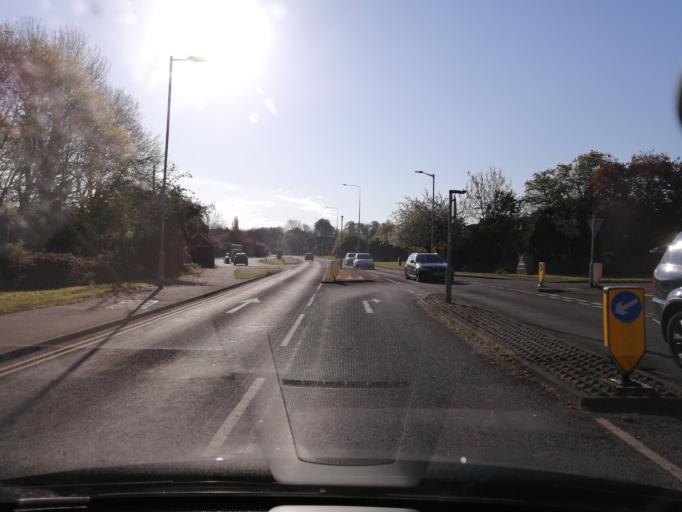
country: GB
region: England
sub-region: Peterborough
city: Peterborough
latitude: 52.5550
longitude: -0.2950
